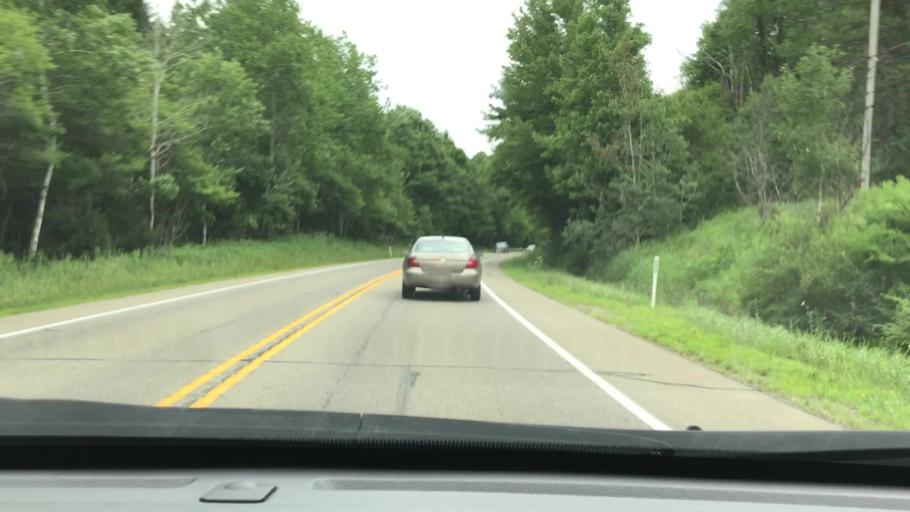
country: US
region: Pennsylvania
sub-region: Elk County
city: Johnsonburg
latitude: 41.5172
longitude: -78.6798
